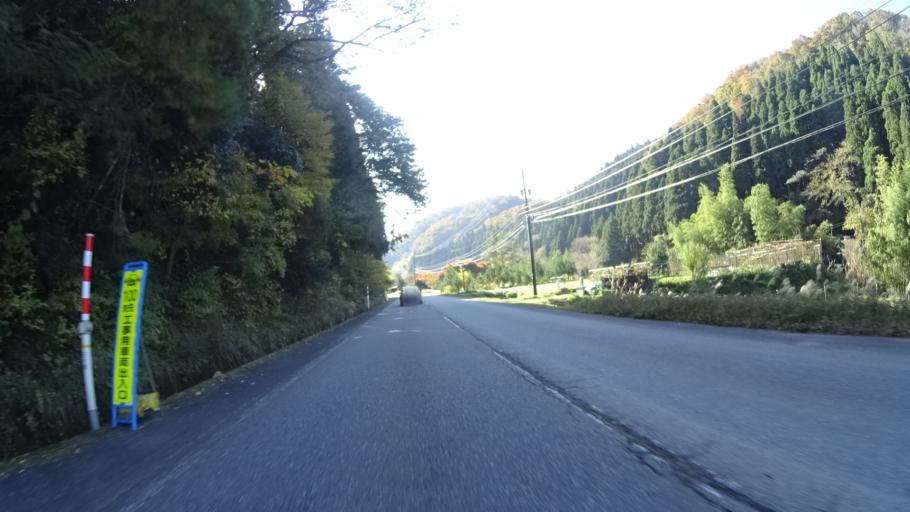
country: JP
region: Ishikawa
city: Komatsu
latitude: 36.3764
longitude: 136.5421
